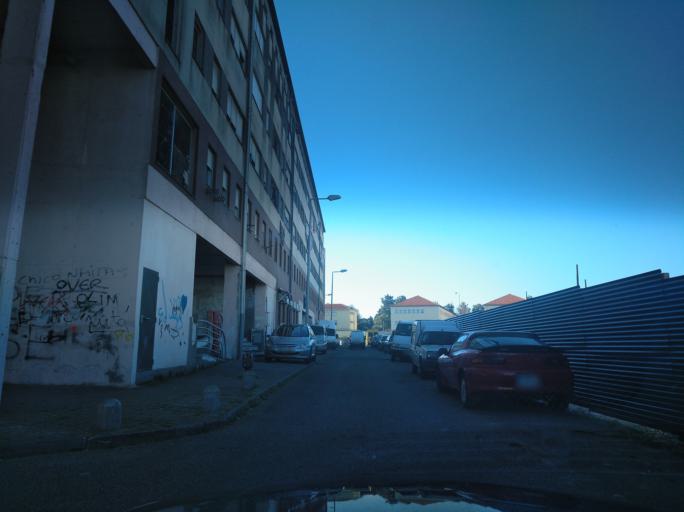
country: PT
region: Lisbon
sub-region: Loures
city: Sacavem
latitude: 38.7814
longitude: -9.1174
